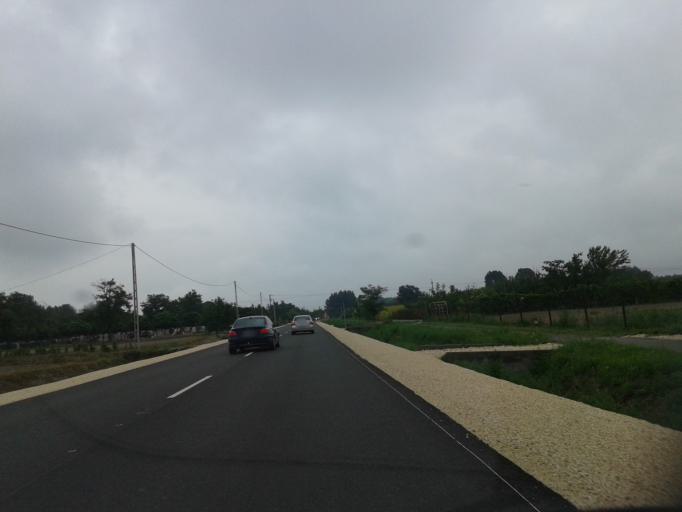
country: HU
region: Csongrad
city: Domaszek
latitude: 46.2432
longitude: 20.0242
